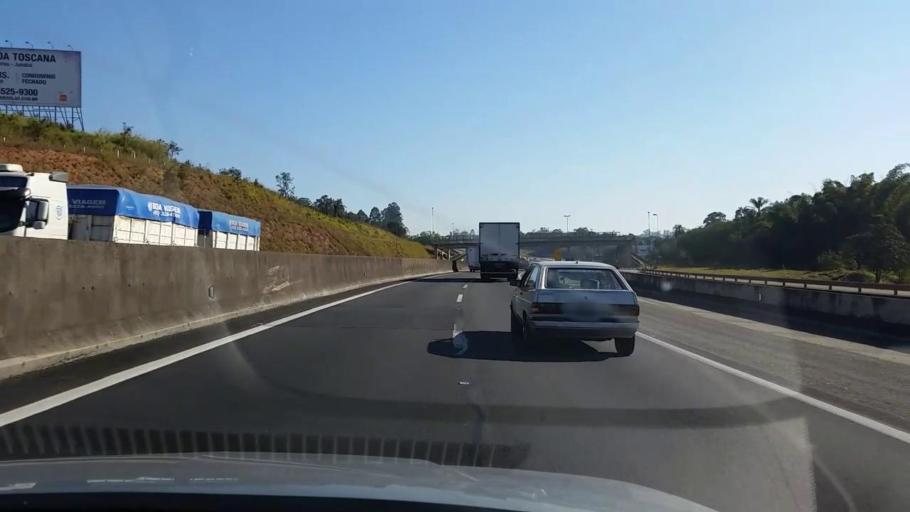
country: BR
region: Sao Paulo
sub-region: Varzea Paulista
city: Varzea Paulista
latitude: -23.2428
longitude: -46.8686
